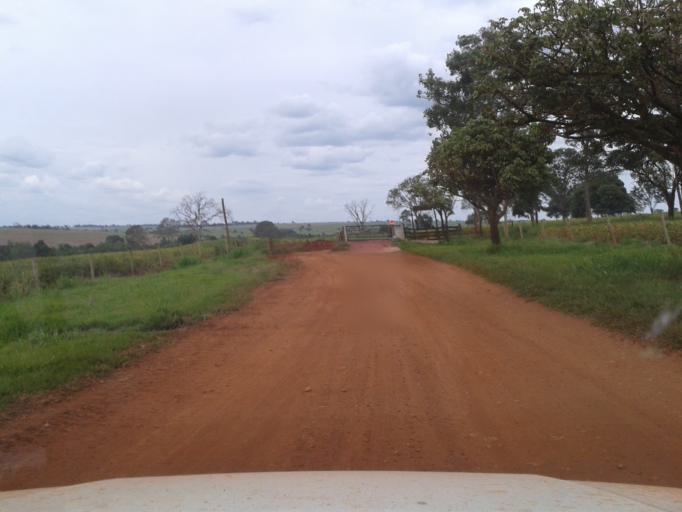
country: BR
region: Minas Gerais
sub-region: Centralina
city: Centralina
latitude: -18.7734
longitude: -49.2215
